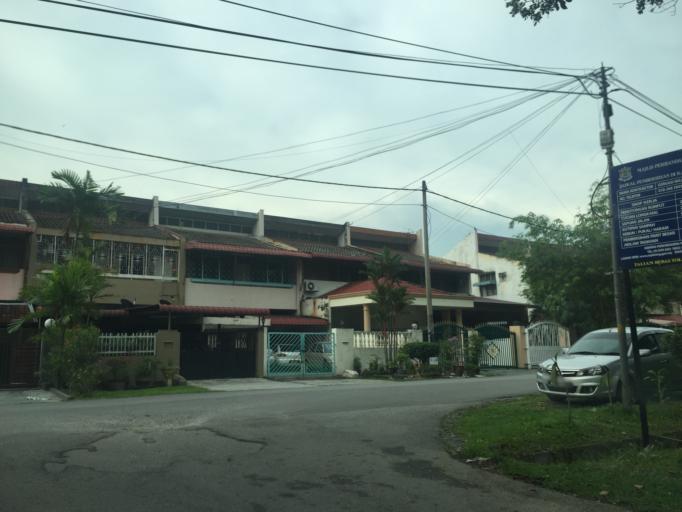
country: MY
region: Selangor
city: Klang
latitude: 3.0054
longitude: 101.4451
